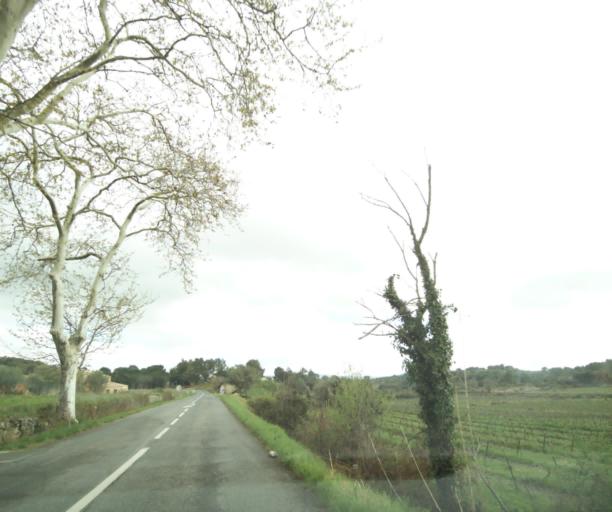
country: FR
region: Languedoc-Roussillon
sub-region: Departement de l'Herault
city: Murviel-les-Montpellier
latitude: 43.5977
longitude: 3.7445
